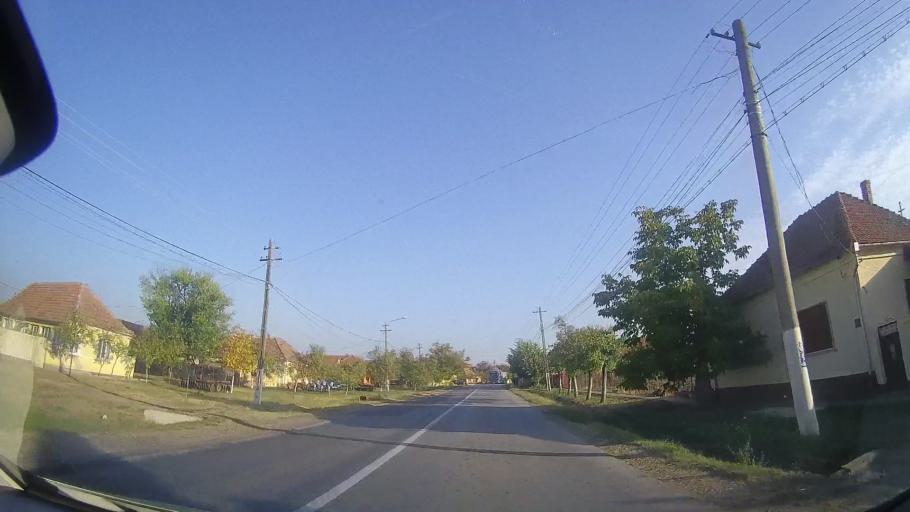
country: RO
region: Timis
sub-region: Comuna Fibis
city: Fibis
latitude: 45.9663
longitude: 21.4179
